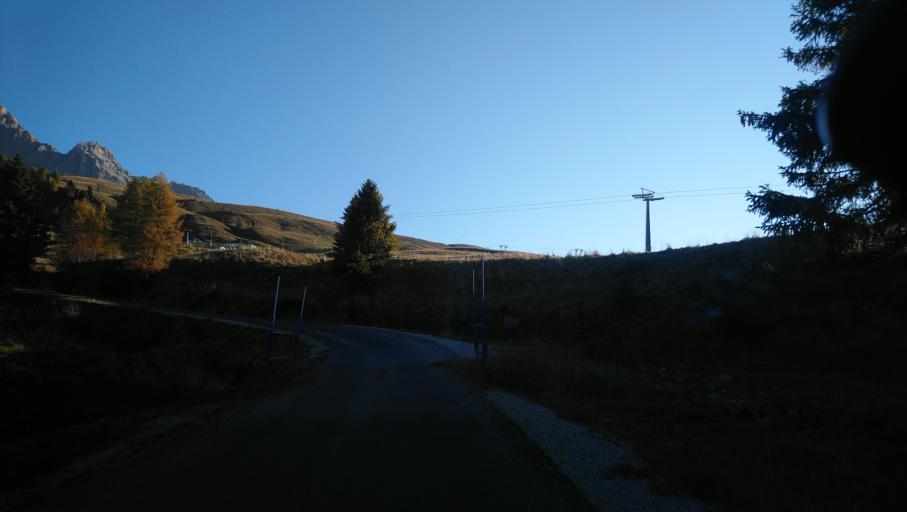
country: IT
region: Veneto
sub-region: Provincia di Belluno
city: Falcade Alto
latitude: 46.3823
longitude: 11.7947
